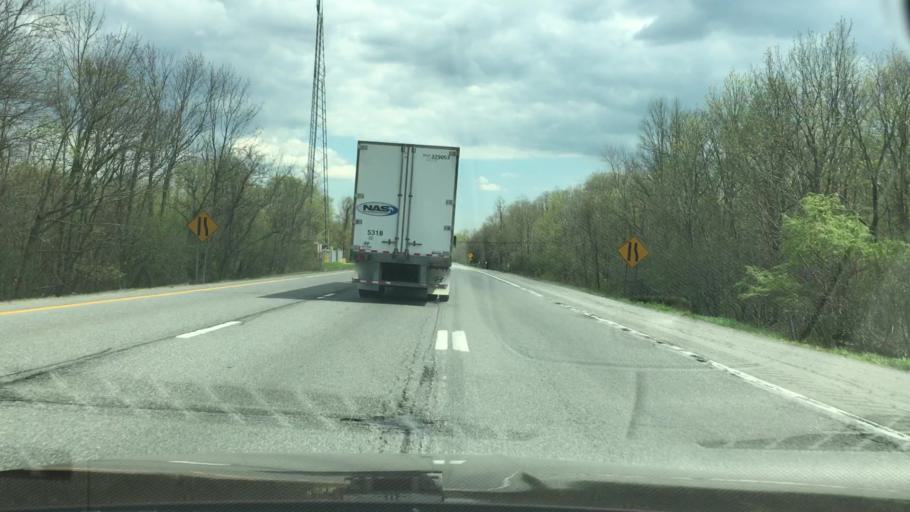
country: US
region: New York
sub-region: Putnam County
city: Lake Carmel
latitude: 41.5412
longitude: -73.7122
